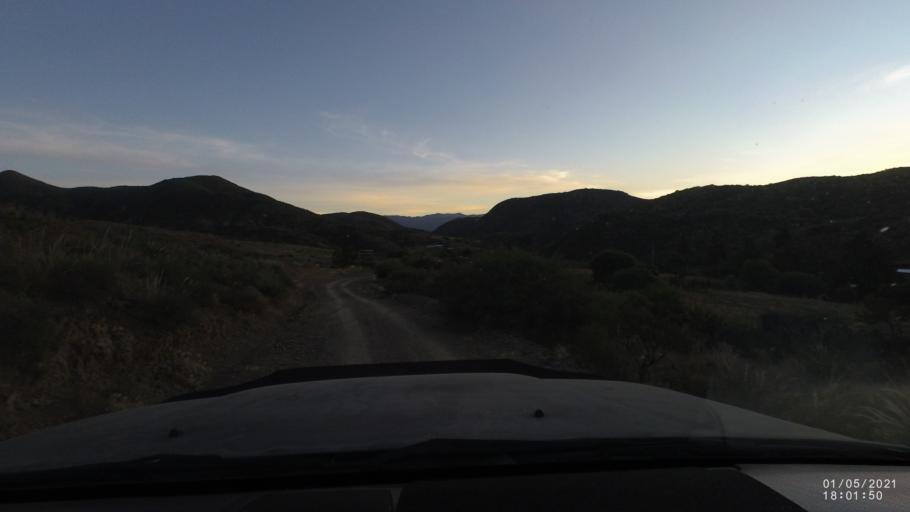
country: BO
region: Cochabamba
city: Capinota
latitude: -17.6858
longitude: -66.1722
